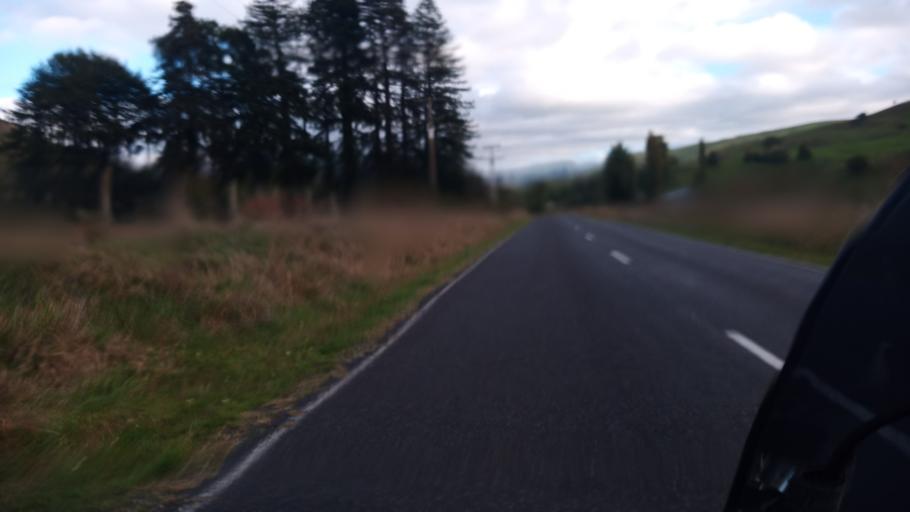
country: NZ
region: Gisborne
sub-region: Gisborne District
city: Gisborne
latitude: -38.5846
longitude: 177.7535
